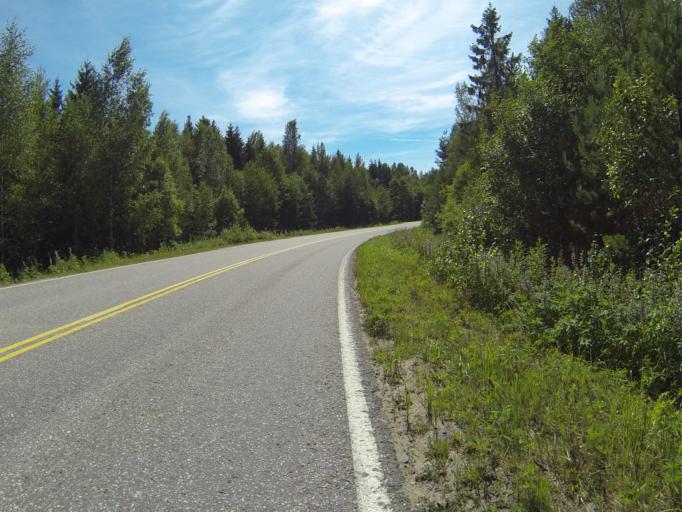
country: FI
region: Varsinais-Suomi
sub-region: Salo
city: Saerkisalo
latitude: 60.2652
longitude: 22.9737
